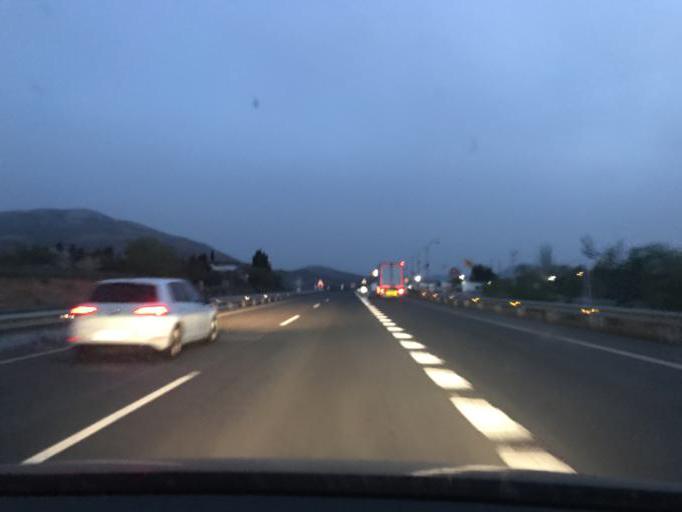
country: ES
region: Andalusia
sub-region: Provincia de Granada
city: Gor
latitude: 37.4168
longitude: -2.9184
